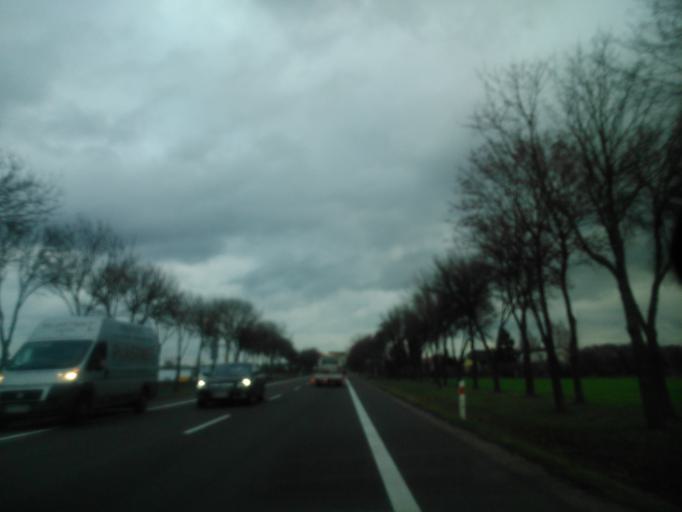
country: PL
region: Masovian Voivodeship
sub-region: Powiat plonski
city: Plonsk
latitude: 52.6070
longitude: 20.3851
